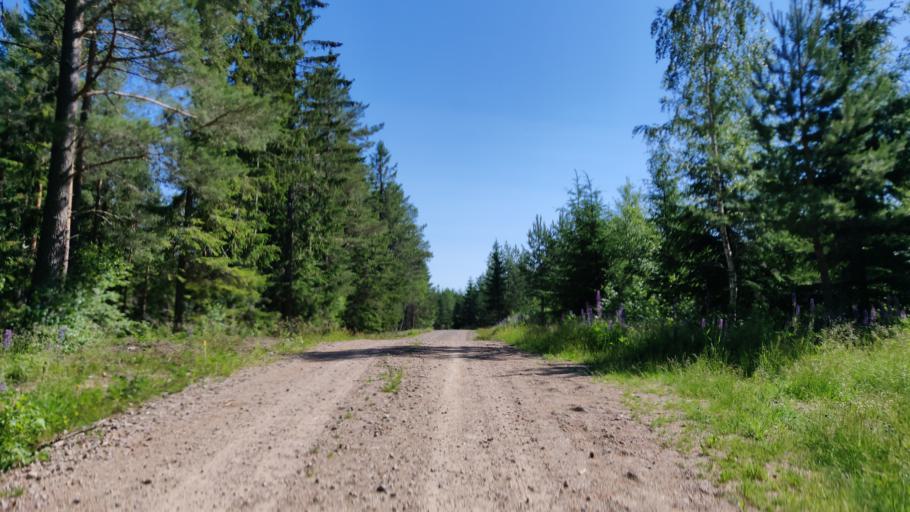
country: SE
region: Vaermland
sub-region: Hagfors Kommun
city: Hagfors
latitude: 59.9879
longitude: 13.5977
